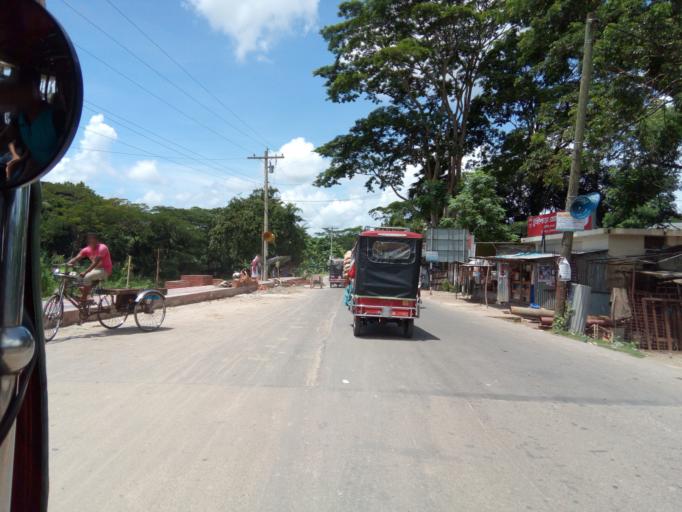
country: BD
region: Dhaka
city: Tungipara
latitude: 22.8949
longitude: 89.8903
